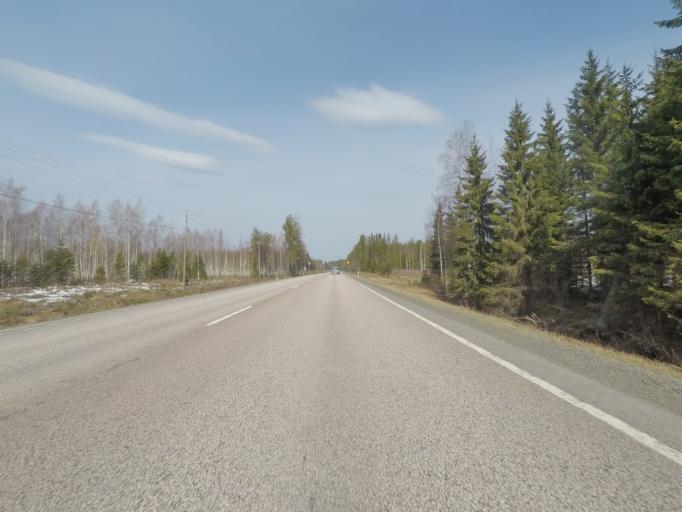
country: FI
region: Central Finland
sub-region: Joutsa
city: Leivonmaeki
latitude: 61.9299
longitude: 26.1151
